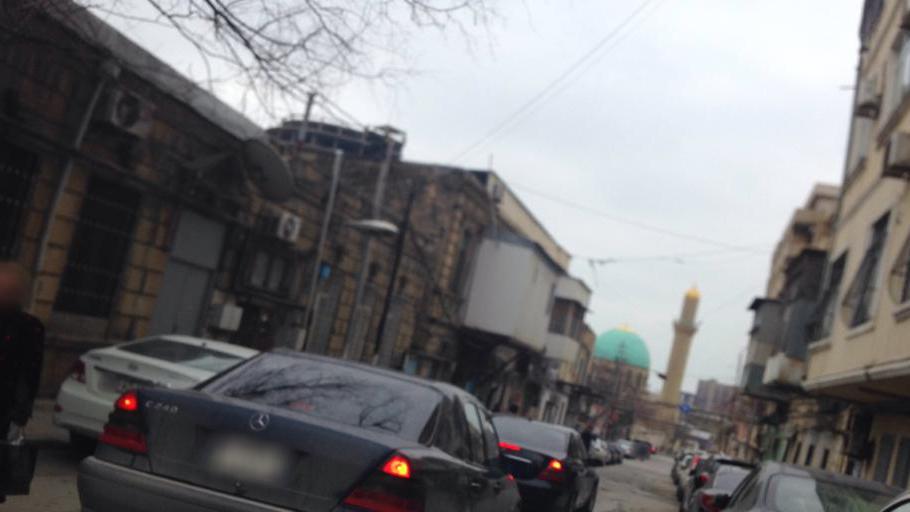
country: AZ
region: Baki
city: Badamdar
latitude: 40.3804
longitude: 49.8287
